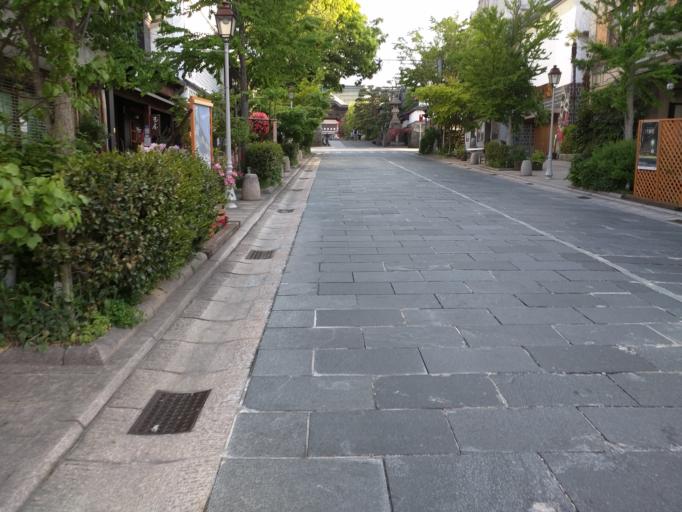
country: JP
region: Nagano
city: Nagano-shi
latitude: 36.6570
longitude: 138.1875
